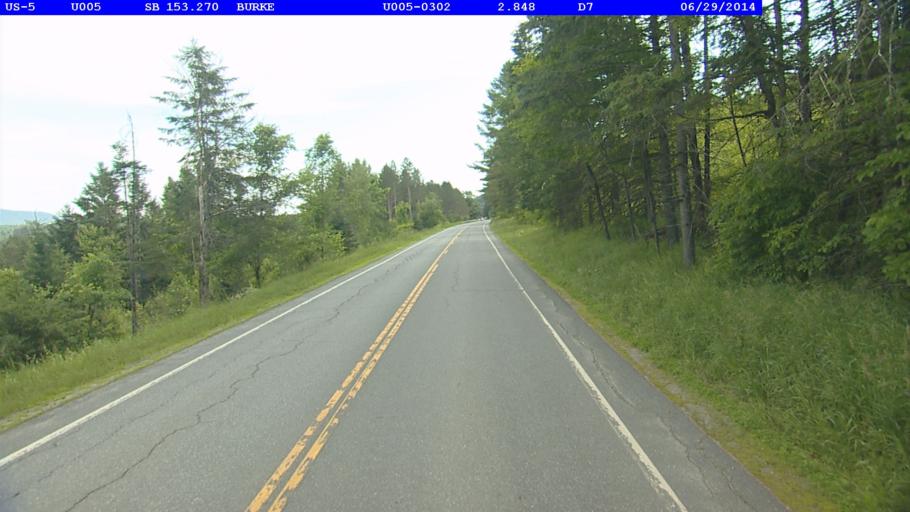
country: US
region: Vermont
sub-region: Caledonia County
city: Lyndonville
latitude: 44.6257
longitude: -71.9701
